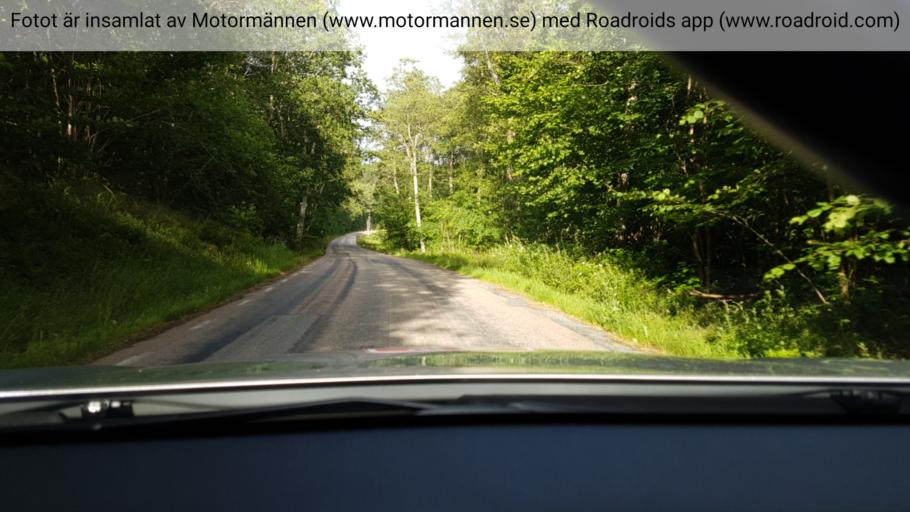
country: SE
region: Vaestra Goetaland
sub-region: Tjorns Kommun
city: Myggenas
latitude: 58.1264
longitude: 11.6796
